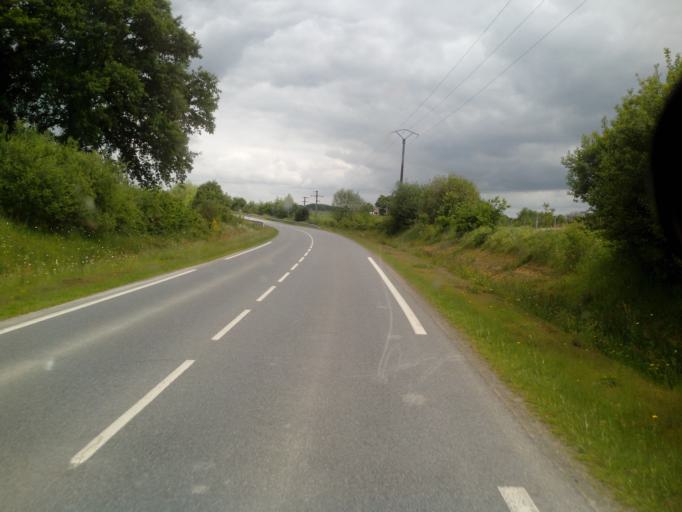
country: FR
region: Brittany
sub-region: Departement d'Ille-et-Vilaine
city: Chasne-sur-Illet
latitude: 48.2547
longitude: -1.6005
